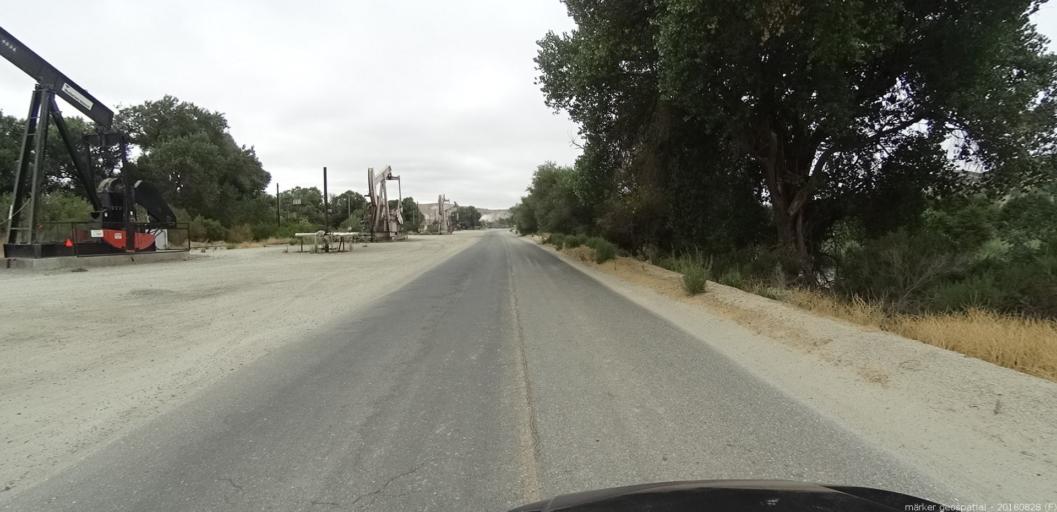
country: US
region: California
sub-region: San Luis Obispo County
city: Lake Nacimiento
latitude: 35.9585
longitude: -120.8784
